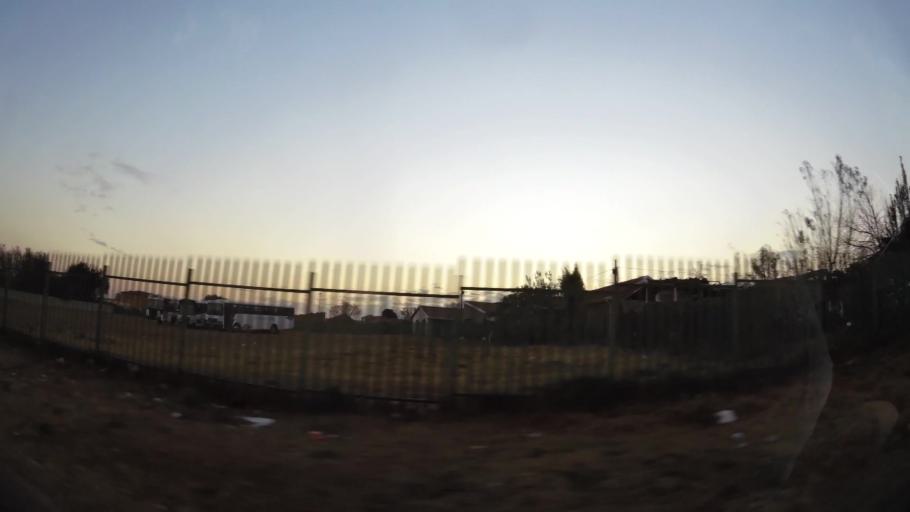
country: ZA
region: Gauteng
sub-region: West Rand District Municipality
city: Randfontein
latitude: -26.2102
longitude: 27.7139
